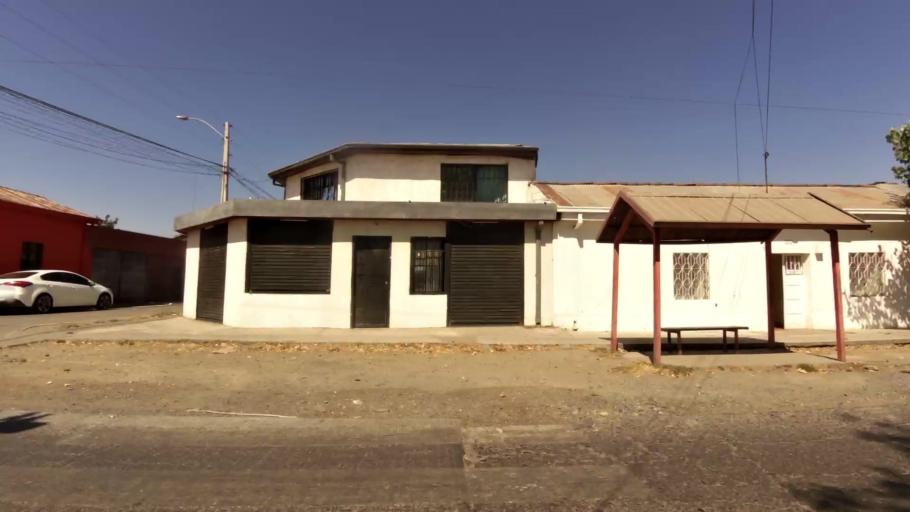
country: CL
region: Maule
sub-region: Provincia de Talca
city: Talca
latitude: -35.4376
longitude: -71.6513
